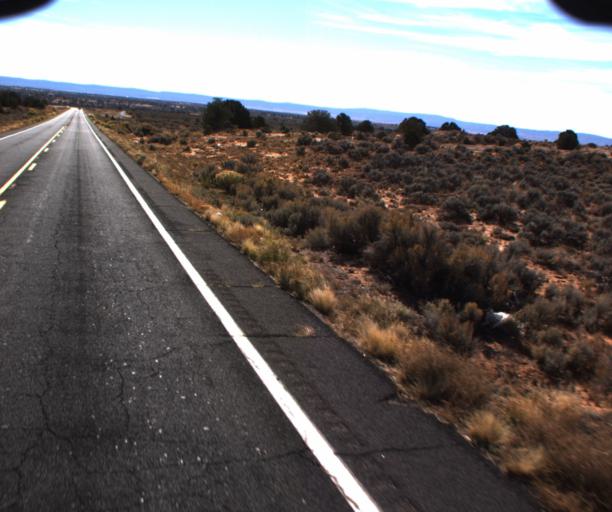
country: US
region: Arizona
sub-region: Coconino County
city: Kaibito
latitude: 36.5650
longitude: -110.7570
